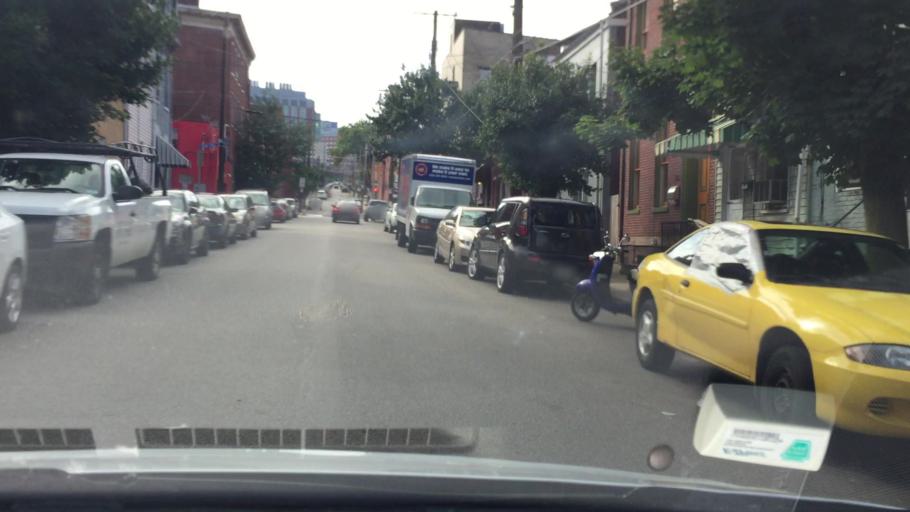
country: US
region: Pennsylvania
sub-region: Allegheny County
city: Bloomfield
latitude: 40.4720
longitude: -79.9606
